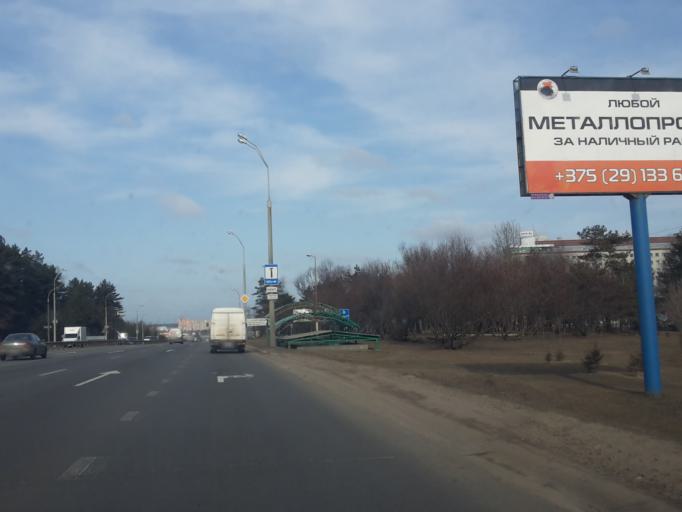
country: BY
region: Minsk
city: Borovlyany
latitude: 53.9237
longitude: 27.6805
